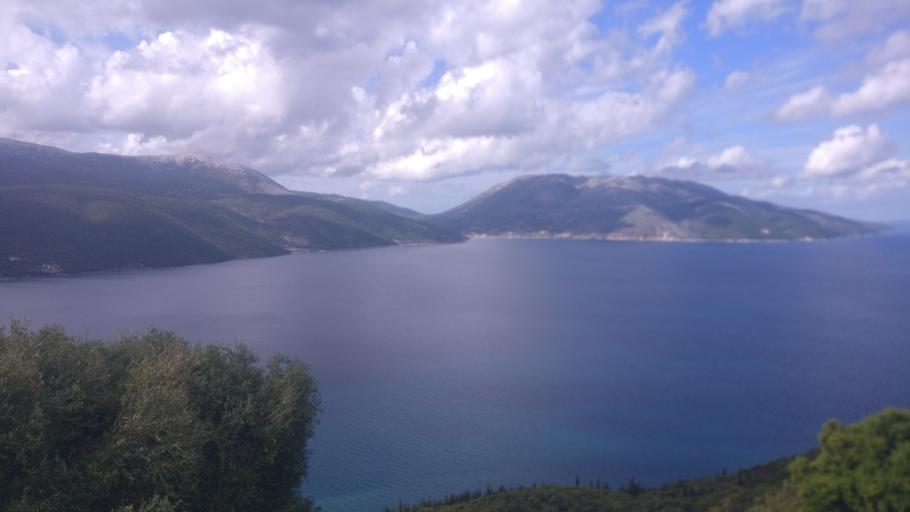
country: GR
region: Ionian Islands
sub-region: Nomos Kefallinias
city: Sami
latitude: 38.2548
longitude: 20.6596
